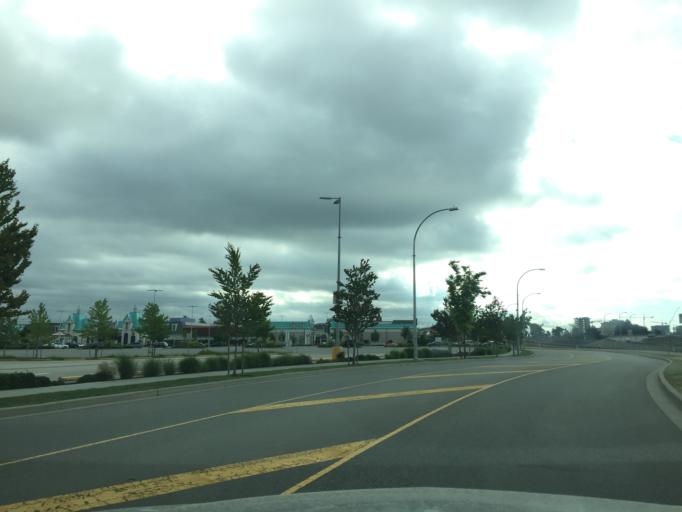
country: CA
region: British Columbia
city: Richmond
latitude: 49.1974
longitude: -123.1448
